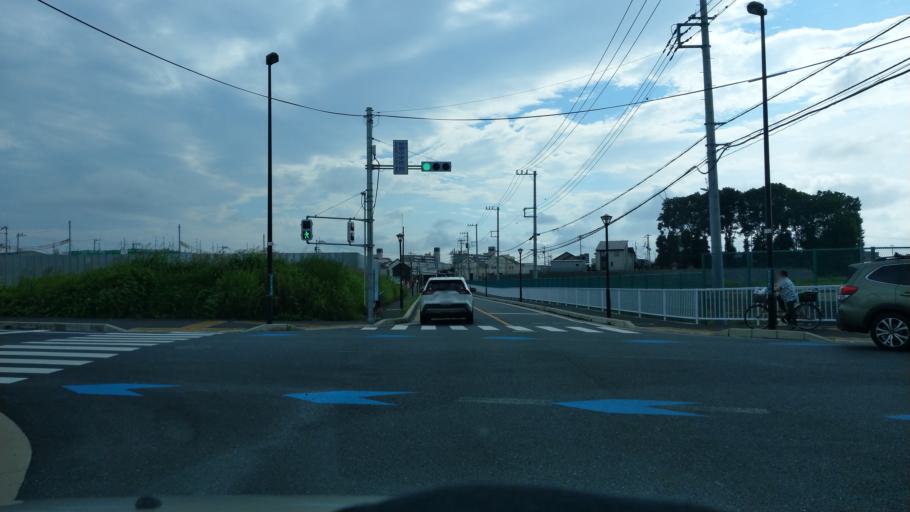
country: JP
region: Saitama
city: Ageoshimo
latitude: 35.9264
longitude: 139.5758
